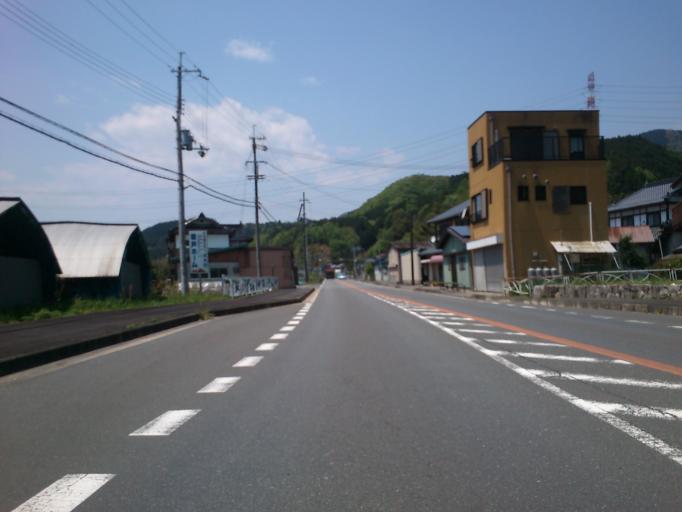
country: JP
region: Kyoto
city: Fukuchiyama
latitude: 35.3250
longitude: 135.0425
